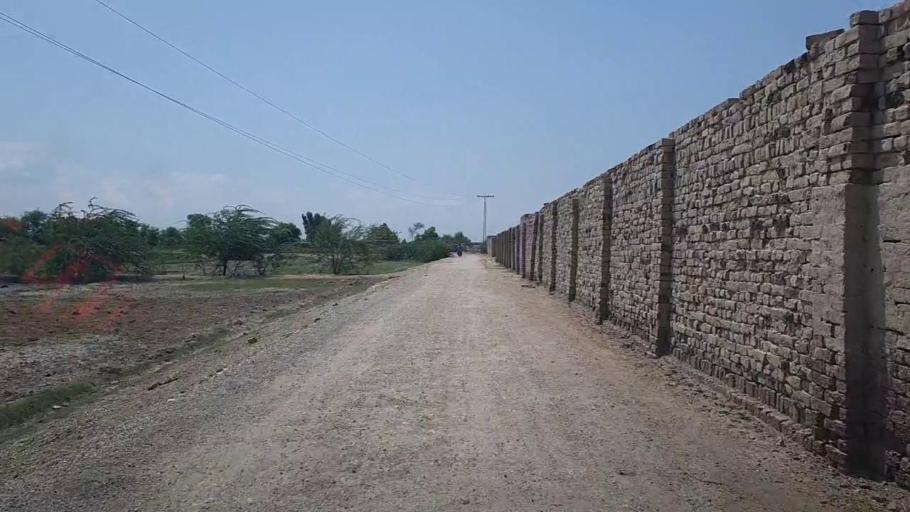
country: PK
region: Sindh
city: Ubauro
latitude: 28.1708
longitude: 69.7627
